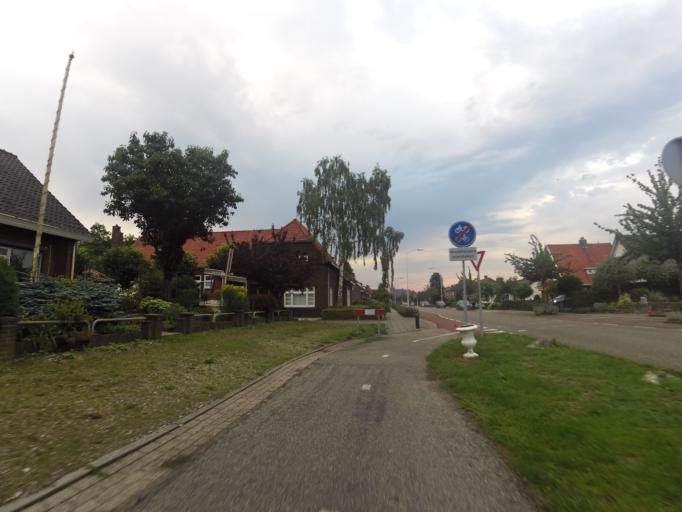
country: NL
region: Gelderland
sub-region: Oude IJsselstreek
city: Gendringen
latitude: 51.9138
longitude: 6.3454
